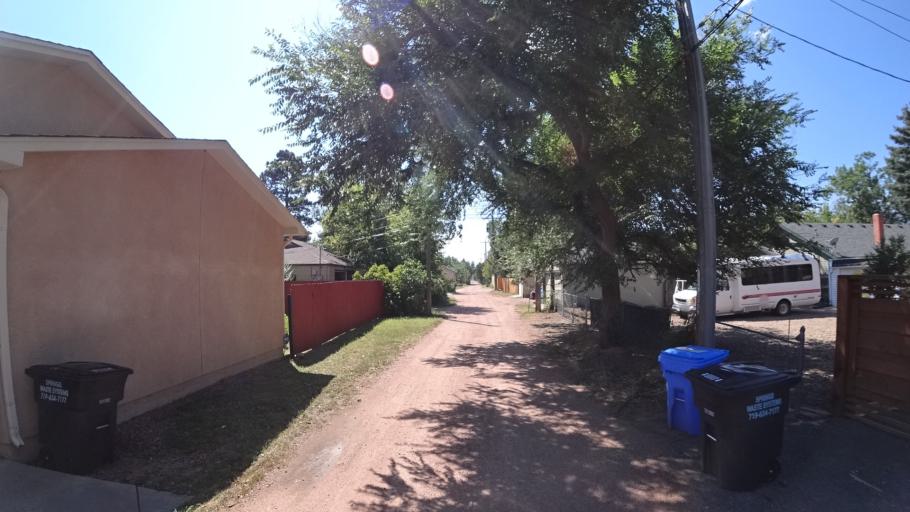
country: US
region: Colorado
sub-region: El Paso County
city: Colorado Springs
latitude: 38.8626
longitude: -104.8140
